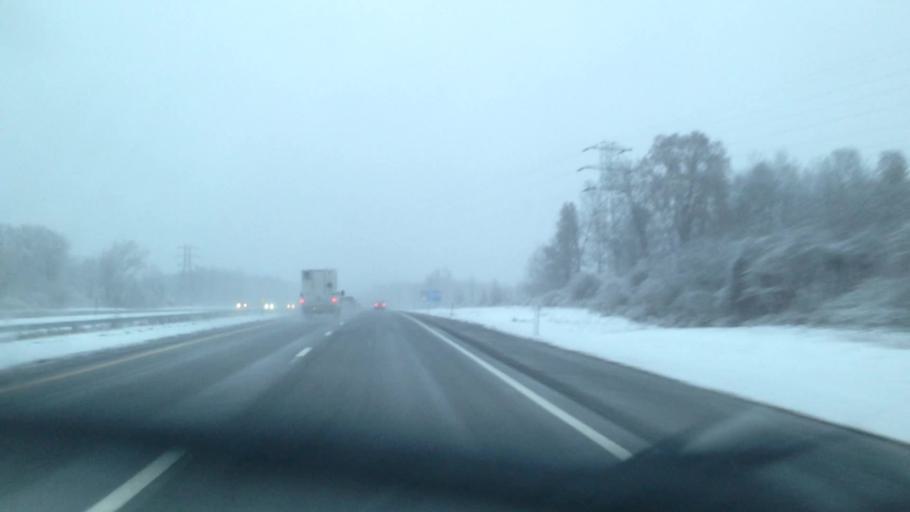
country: US
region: New York
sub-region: Madison County
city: Canastota
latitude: 43.0912
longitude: -75.7751
